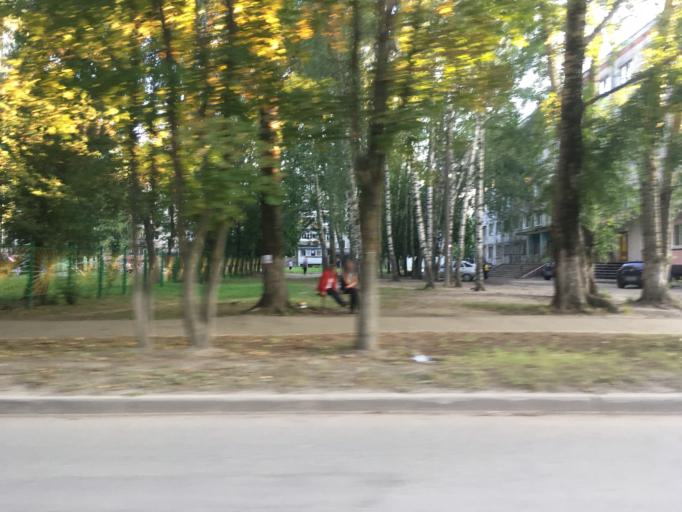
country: RU
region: Mariy-El
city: Yoshkar-Ola
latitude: 56.6485
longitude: 47.8776
